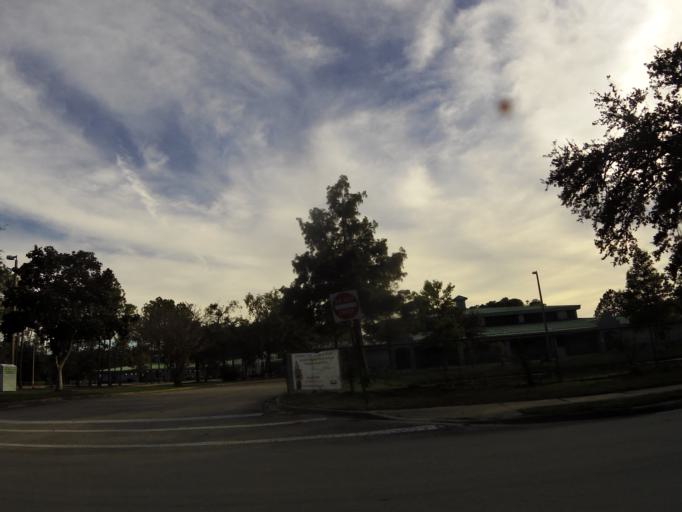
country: US
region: Florida
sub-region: Saint Johns County
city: Fruit Cove
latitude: 30.1614
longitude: -81.5746
